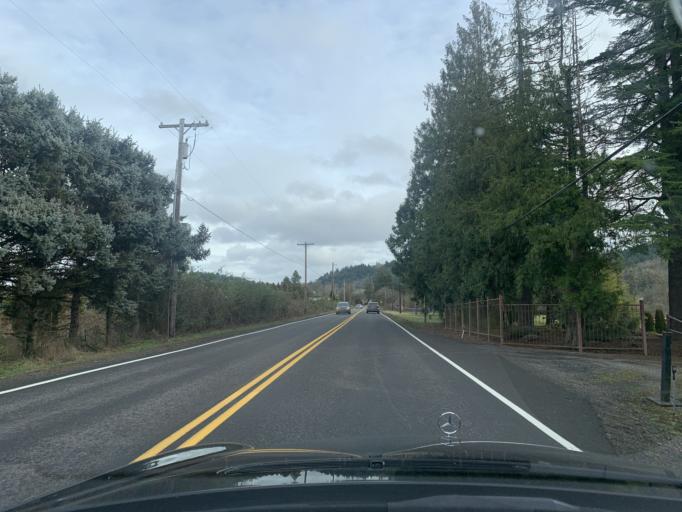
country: US
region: Oregon
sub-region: Multnomah County
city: Gresham
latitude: 45.4674
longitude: -122.4715
